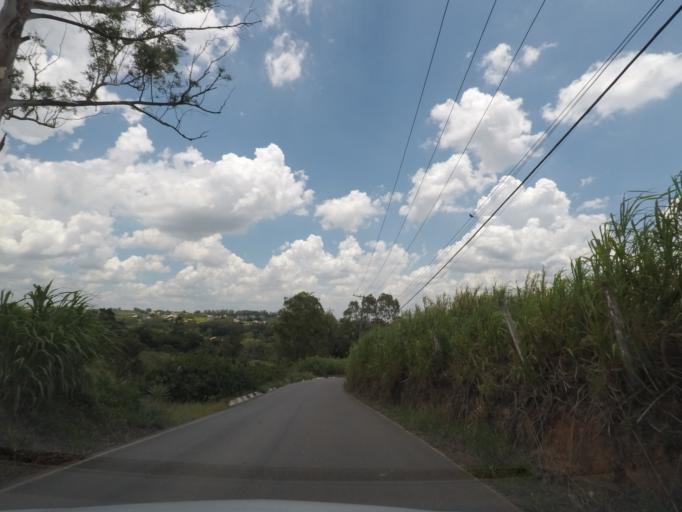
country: BR
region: Sao Paulo
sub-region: Vinhedo
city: Vinhedo
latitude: -23.0704
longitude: -47.0320
